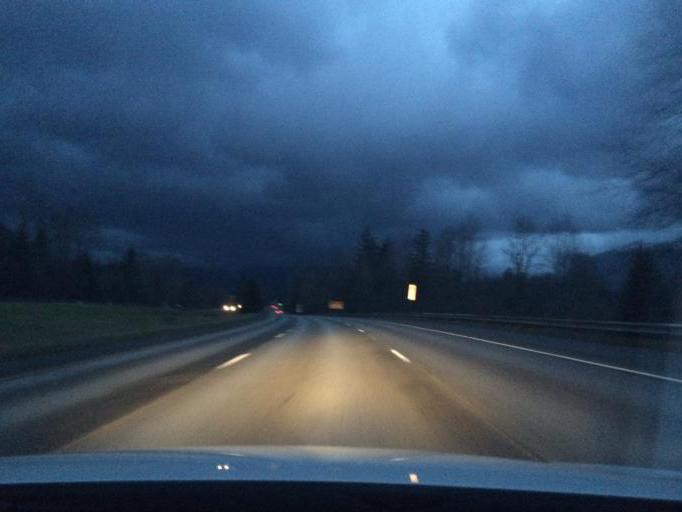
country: US
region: Washington
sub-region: King County
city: North Bend
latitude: 47.4732
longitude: -121.7774
